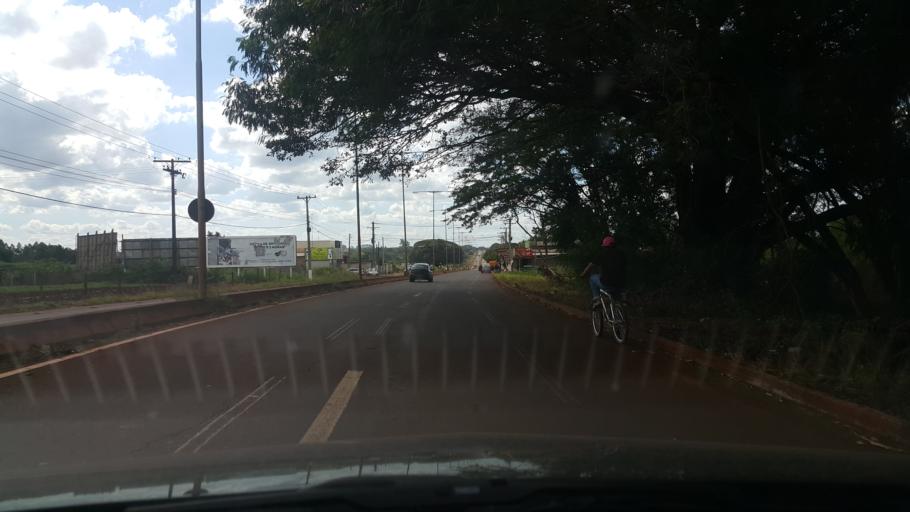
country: BR
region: Mato Grosso do Sul
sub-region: Dourados
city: Dourados
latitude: -22.1986
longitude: -54.8160
